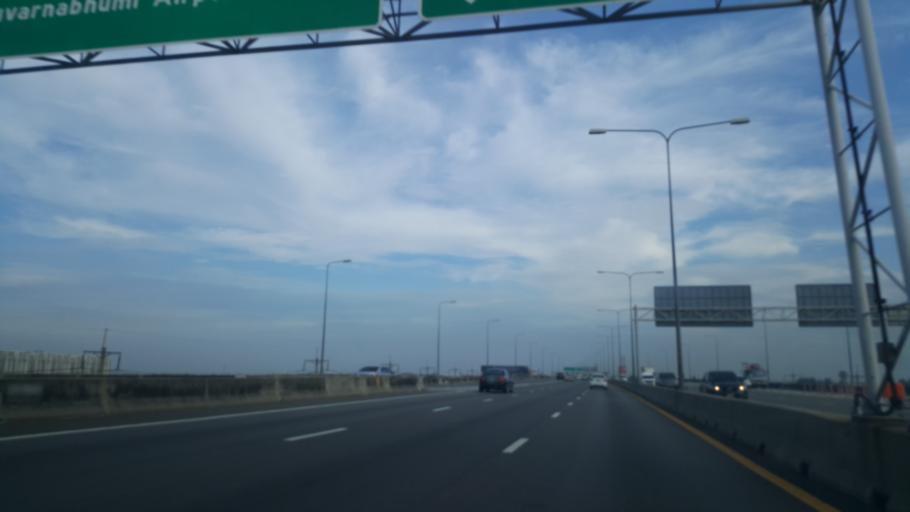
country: TH
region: Bangkok
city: Bang Na
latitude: 13.6283
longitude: 100.7212
